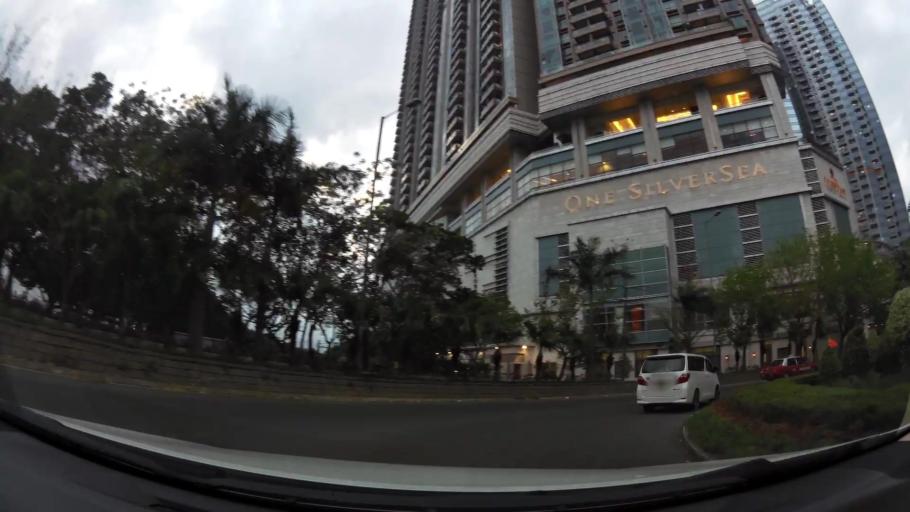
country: HK
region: Sham Shui Po
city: Sham Shui Po
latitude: 22.3172
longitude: 114.1567
